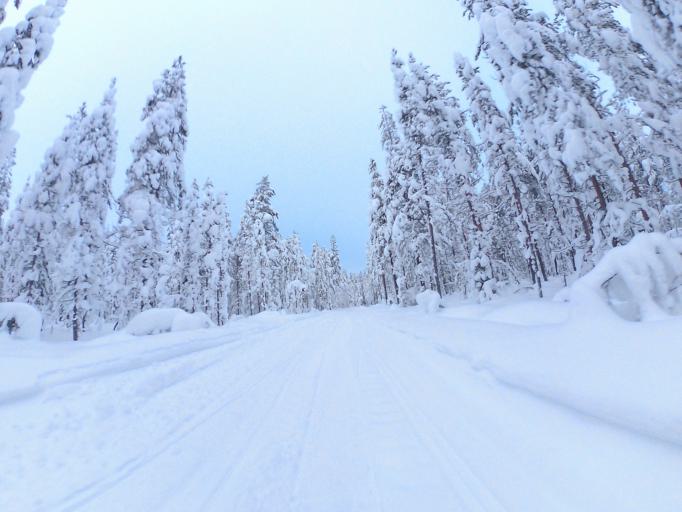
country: FI
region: Lapland
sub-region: Rovaniemi
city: Rovaniemi
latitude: 66.6283
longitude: 26.0380
